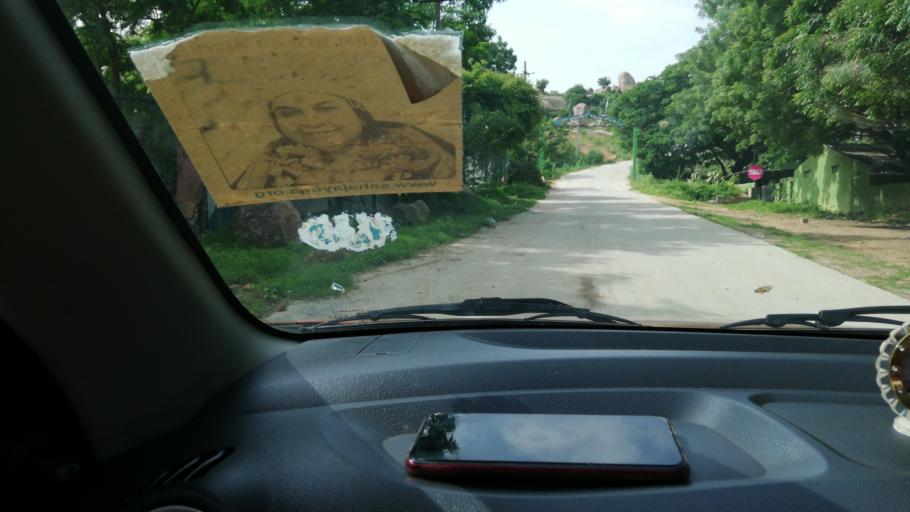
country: IN
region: Telangana
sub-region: Rangareddi
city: Kukatpalli
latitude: 17.4132
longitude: 78.3661
